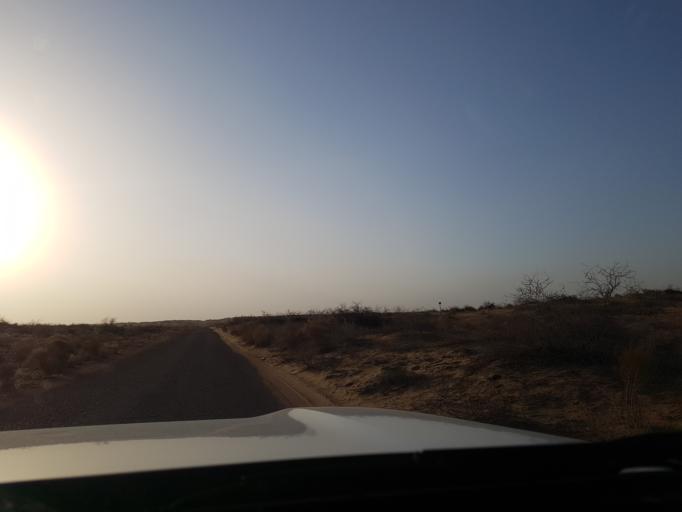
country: UZ
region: Xorazm
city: Khiwa
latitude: 41.1501
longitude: 60.6448
